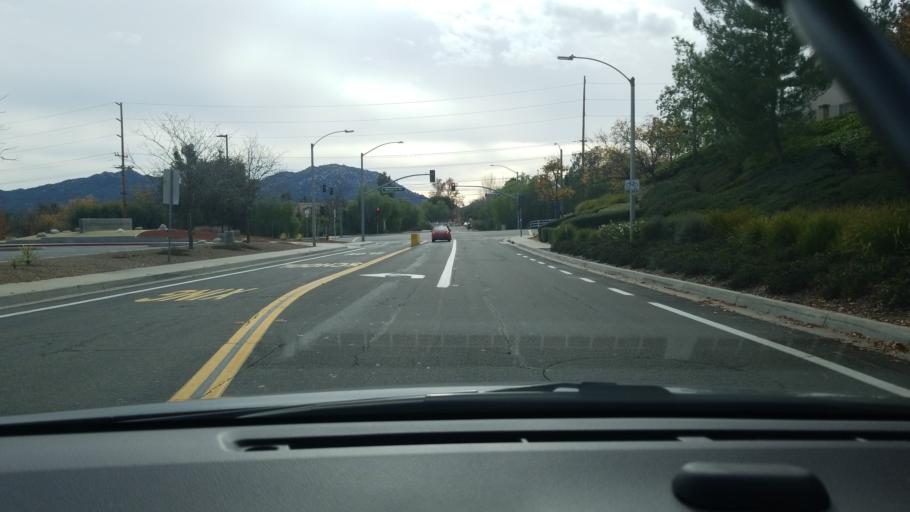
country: US
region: California
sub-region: Riverside County
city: Temecula
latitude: 33.4882
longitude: -117.1048
